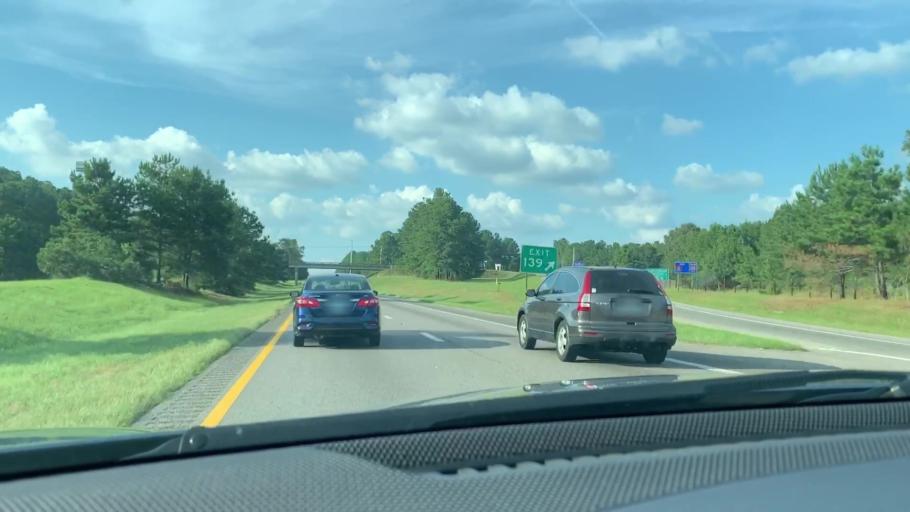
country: US
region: South Carolina
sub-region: Calhoun County
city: Saint Matthews
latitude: 33.6322
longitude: -80.8745
